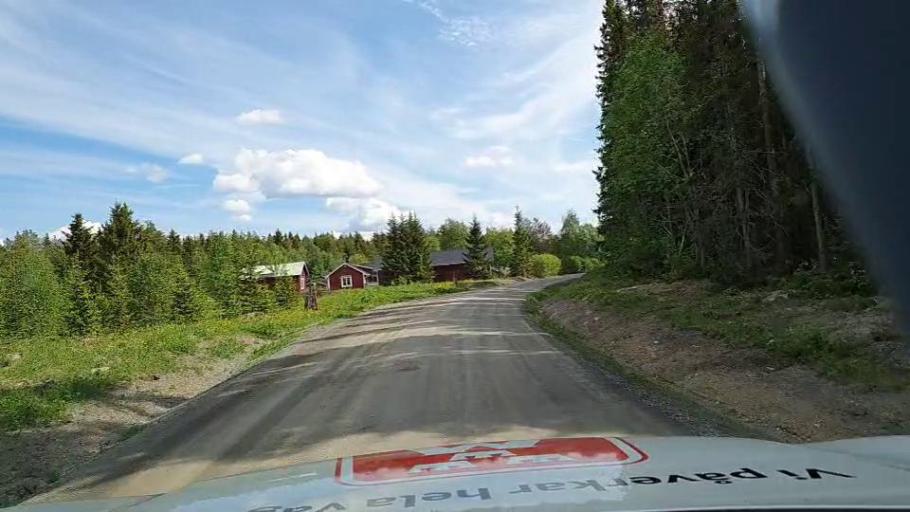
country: SE
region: Jaemtland
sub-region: OEstersunds Kommun
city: Brunflo
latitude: 63.0161
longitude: 14.7744
